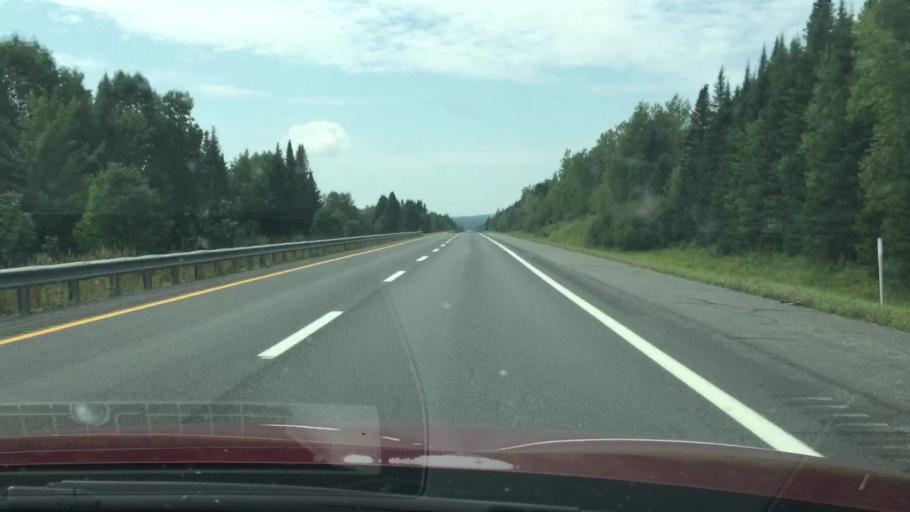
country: US
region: Maine
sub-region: Aroostook County
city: Hodgdon
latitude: 46.1184
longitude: -68.1259
